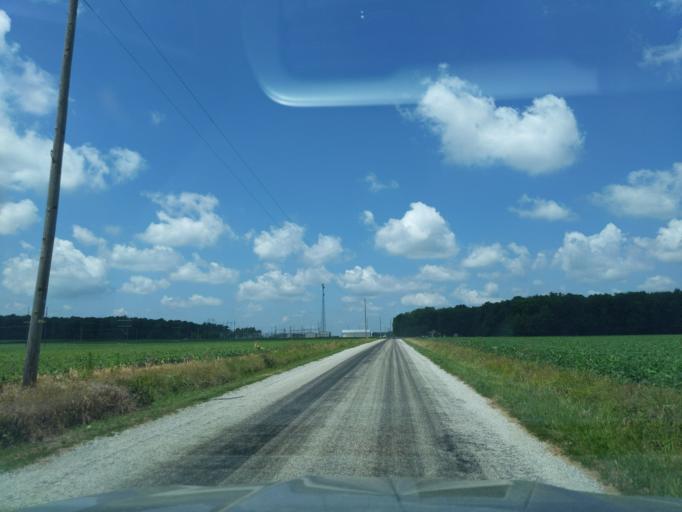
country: US
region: Indiana
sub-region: Ripley County
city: Osgood
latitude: 39.2191
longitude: -85.3369
